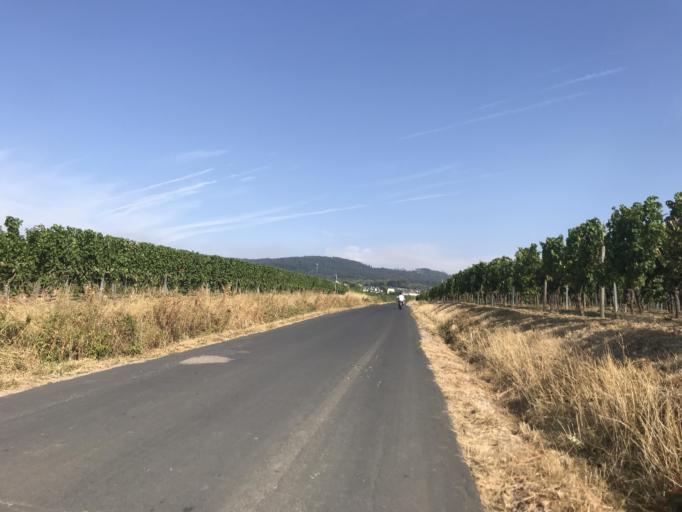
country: DE
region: Rheinland-Pfalz
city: Oestrich-Winkel
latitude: 50.0199
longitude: 8.0333
